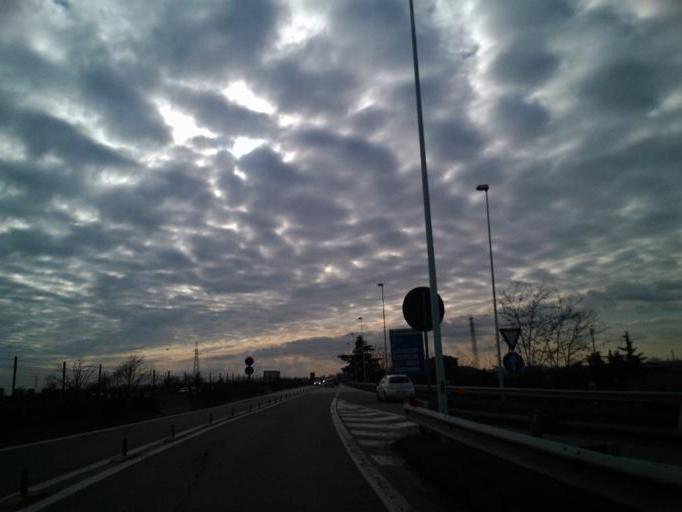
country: IT
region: Veneto
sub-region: Provincia di Verona
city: Monticelli-Fontana
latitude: 45.4193
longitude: 11.1183
